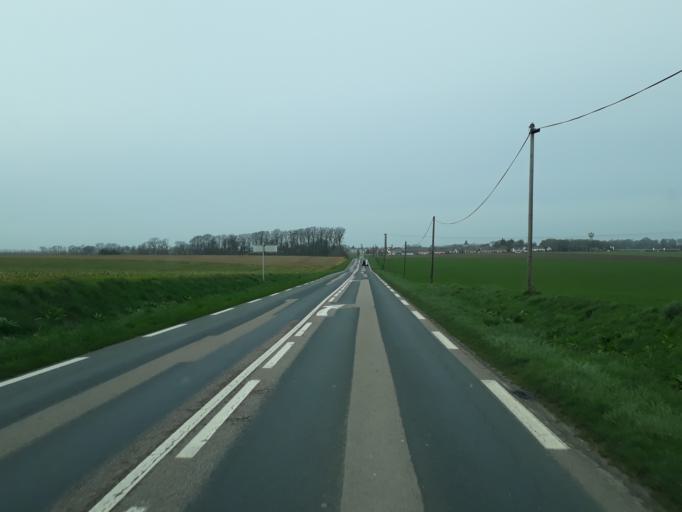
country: FR
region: Haute-Normandie
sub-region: Departement de la Seine-Maritime
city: Breaute
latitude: 49.6159
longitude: 0.4071
